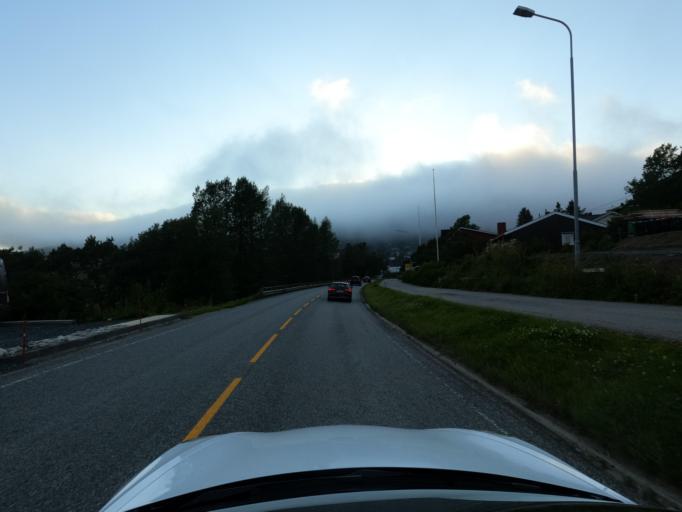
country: NO
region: Troms
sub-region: Harstad
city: Harstad
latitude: 68.8060
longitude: 16.5139
